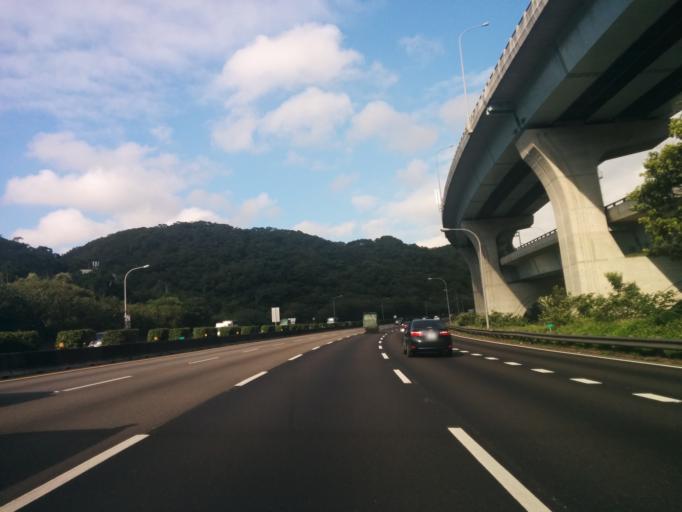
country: TW
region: Taipei
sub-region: Taipei
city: Banqiao
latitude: 25.0558
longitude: 121.4018
